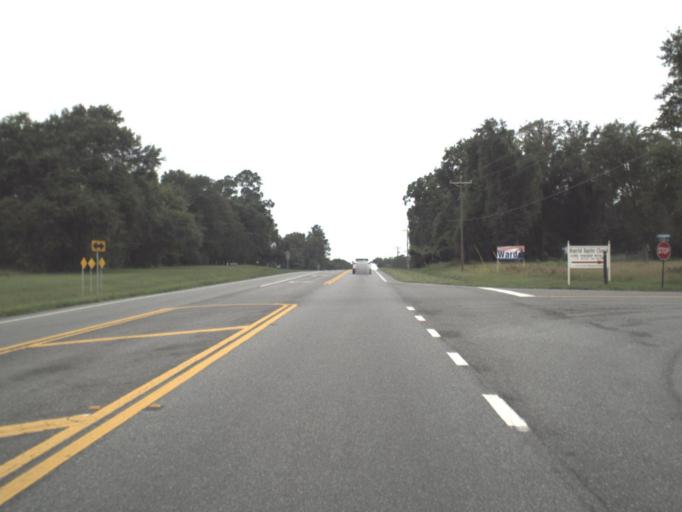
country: US
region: Florida
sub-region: Columbia County
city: Watertown
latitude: 30.1014
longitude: -82.6060
